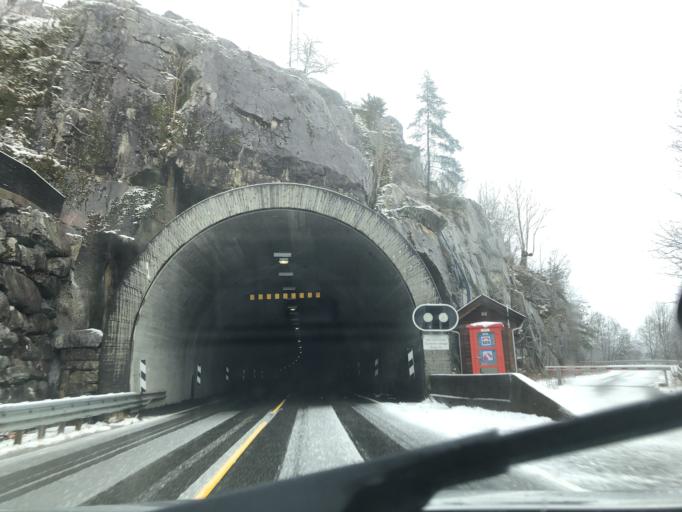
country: NO
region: Rogaland
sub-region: Sauda
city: Sauda
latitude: 59.5297
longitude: 6.5950
